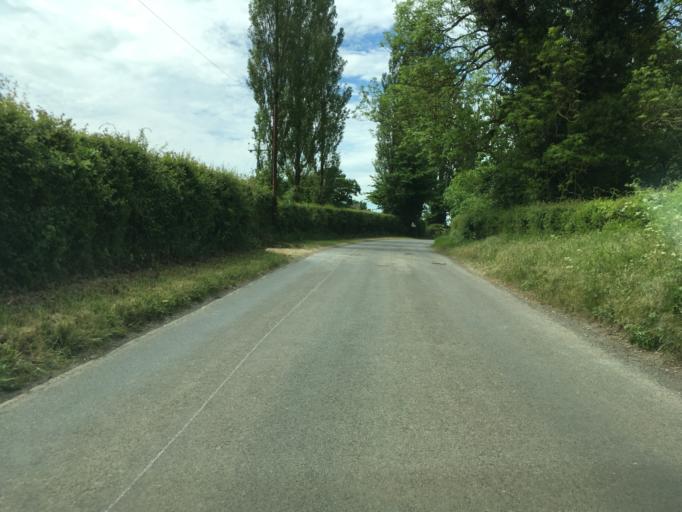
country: GB
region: England
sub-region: South Gloucestershire
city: Charfield
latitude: 51.6662
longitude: -2.4048
